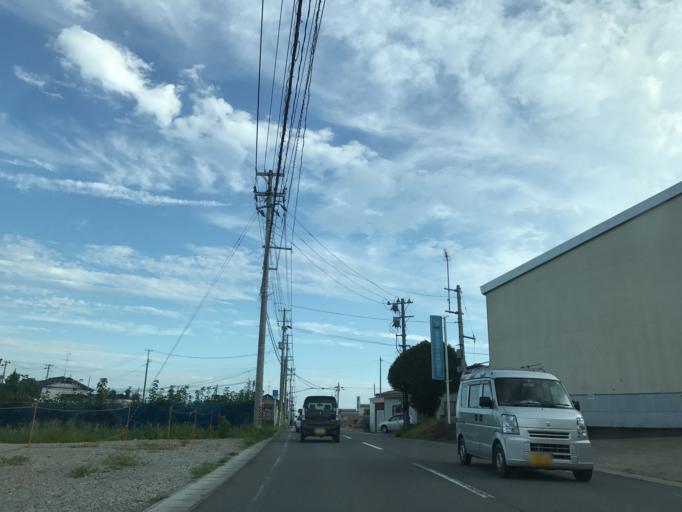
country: JP
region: Fukushima
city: Sukagawa
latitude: 37.3162
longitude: 140.3585
